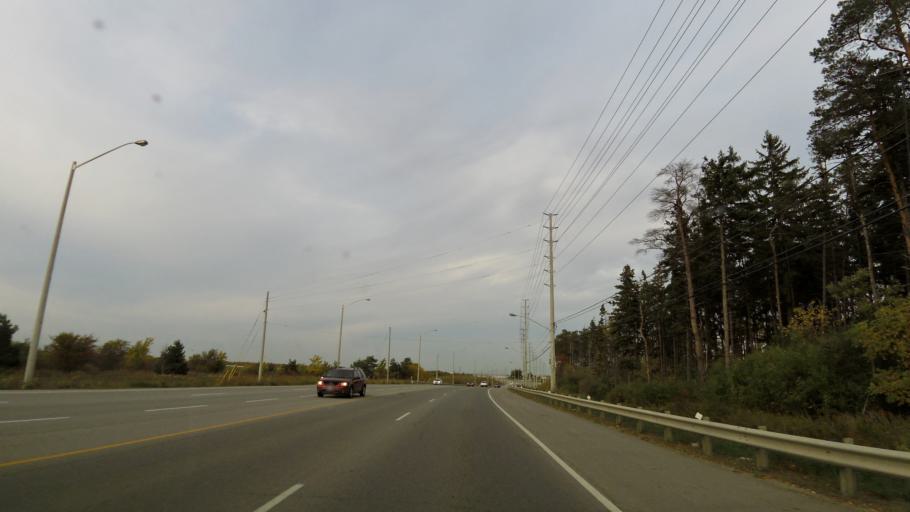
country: CA
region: Ontario
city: Brampton
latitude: 43.7487
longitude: -79.8085
